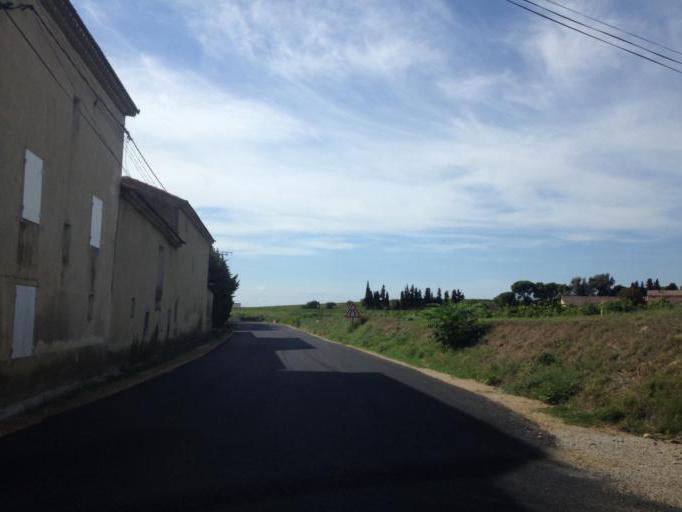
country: FR
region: Provence-Alpes-Cote d'Azur
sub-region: Departement du Vaucluse
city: Courthezon
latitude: 44.0945
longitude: 4.8694
